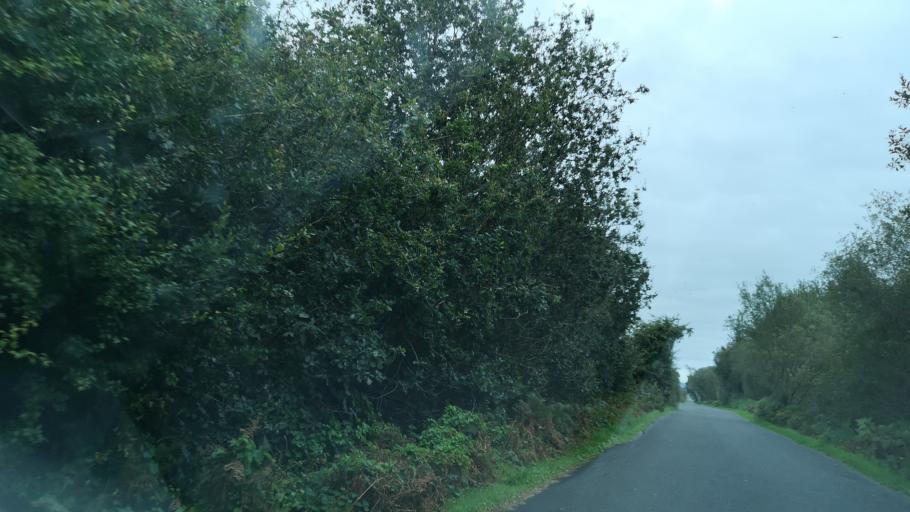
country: IE
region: Leinster
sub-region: Uibh Fhaili
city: Ferbane
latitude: 53.2246
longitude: -7.7281
